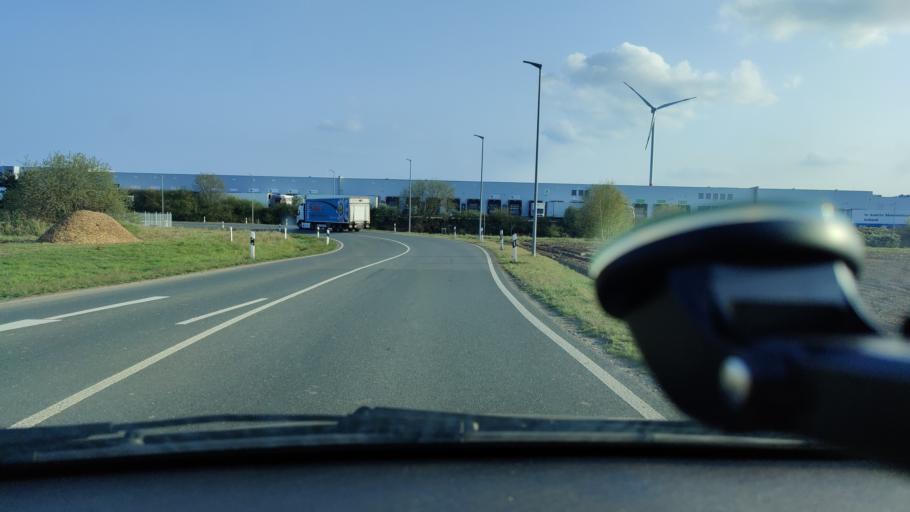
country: DE
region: North Rhine-Westphalia
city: Straelen
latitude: 51.3856
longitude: 6.2375
